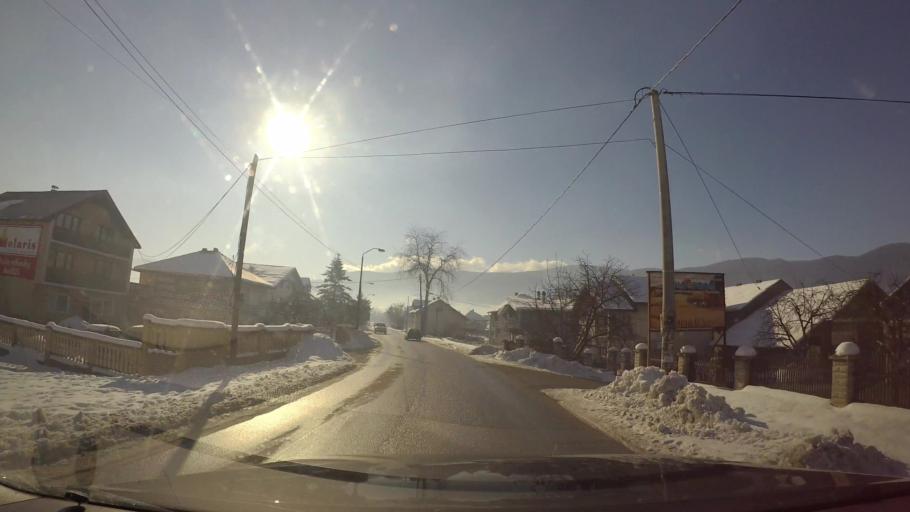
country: BA
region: Federation of Bosnia and Herzegovina
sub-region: Kanton Sarajevo
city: Sarajevo
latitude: 43.8010
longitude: 18.3483
